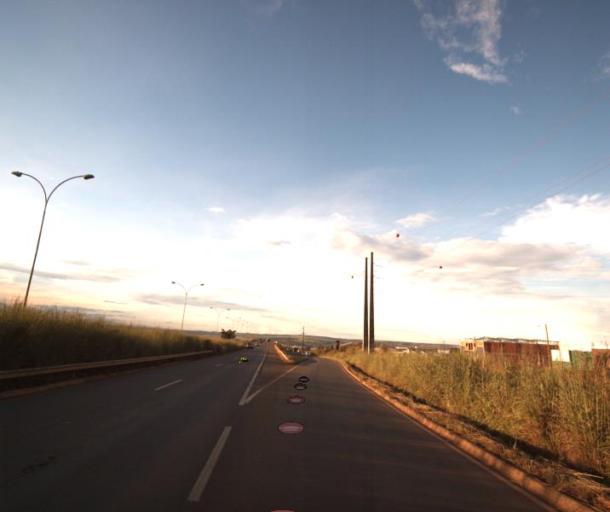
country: BR
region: Goias
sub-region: Anapolis
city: Anapolis
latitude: -16.3280
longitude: -48.9221
